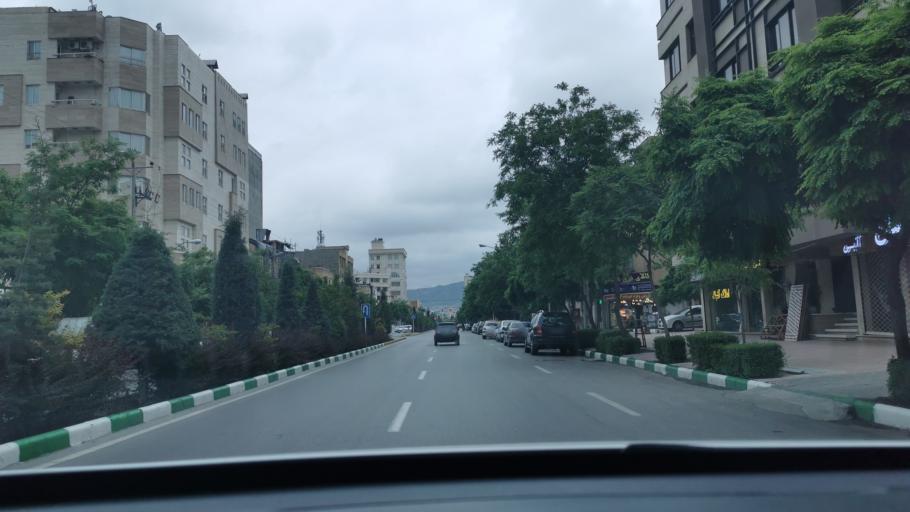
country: IR
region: Razavi Khorasan
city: Mashhad
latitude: 36.3264
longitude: 59.5275
